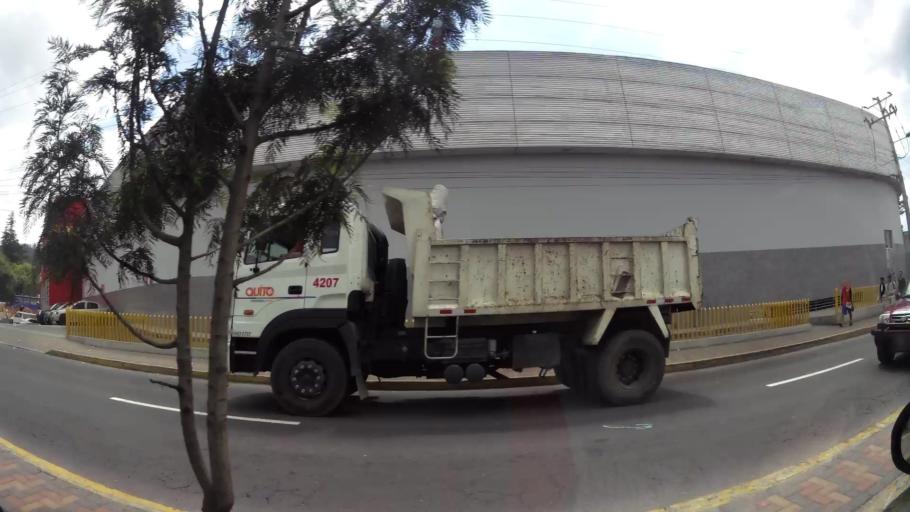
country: EC
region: Pichincha
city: Quito
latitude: -0.1041
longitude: -78.4531
